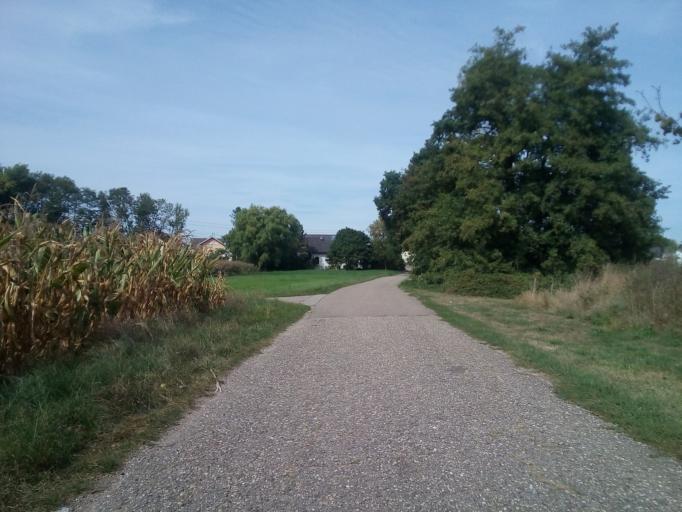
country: DE
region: Baden-Wuerttemberg
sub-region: Karlsruhe Region
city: Ottenhofen
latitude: 48.7351
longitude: 8.1243
